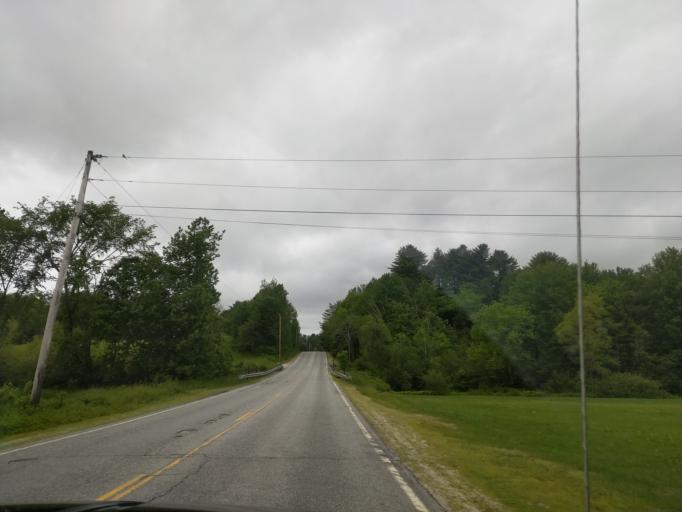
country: US
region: Maine
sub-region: Cumberland County
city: North Windham
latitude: 43.8279
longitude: -70.3943
